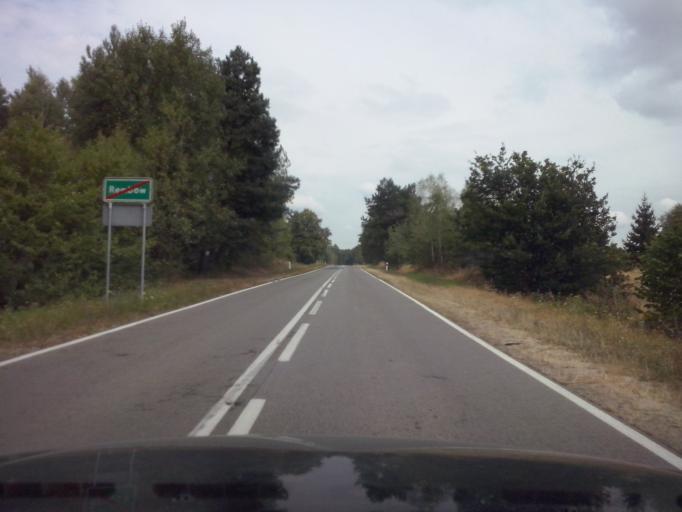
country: PL
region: Swietokrzyskie
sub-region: Powiat kielecki
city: Rakow
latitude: 50.7126
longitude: 21.0599
